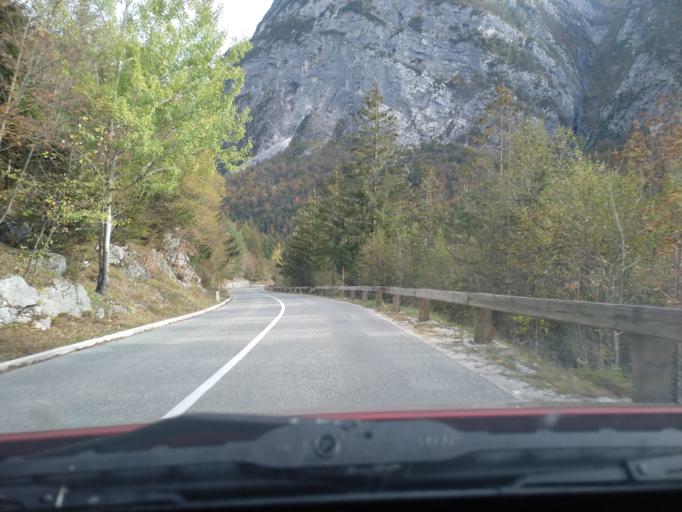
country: SI
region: Kranjska Gora
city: Kranjska Gora
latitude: 46.3842
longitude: 13.7537
